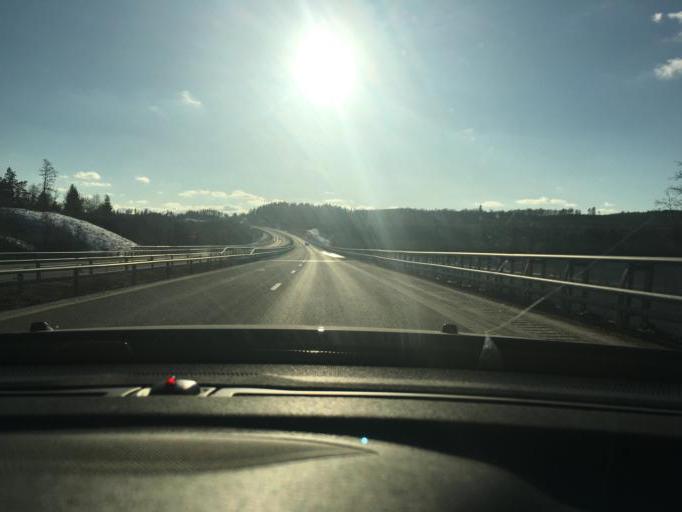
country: SE
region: Vaestra Goetaland
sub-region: Boras Kommun
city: Dalsjofors
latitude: 57.7887
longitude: 13.1300
